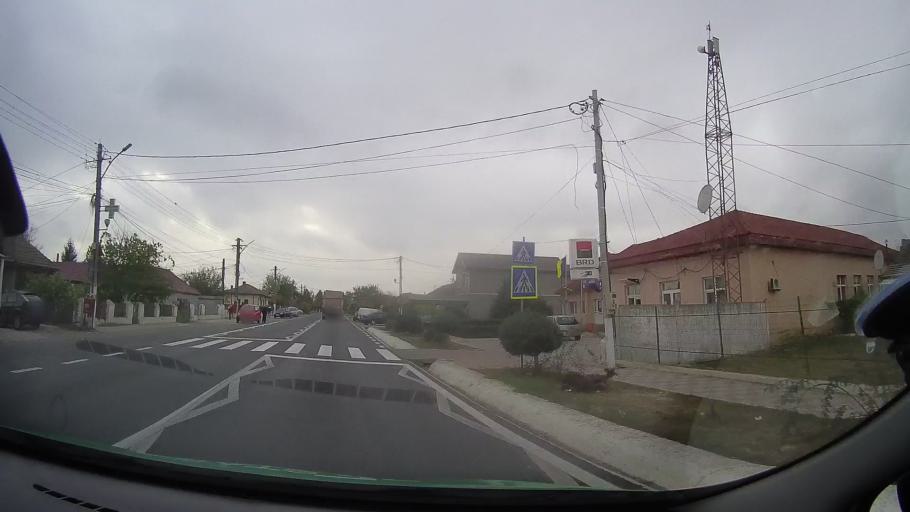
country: RO
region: Constanta
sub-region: Comuna Castelu
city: Castelu
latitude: 44.2556
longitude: 28.3374
